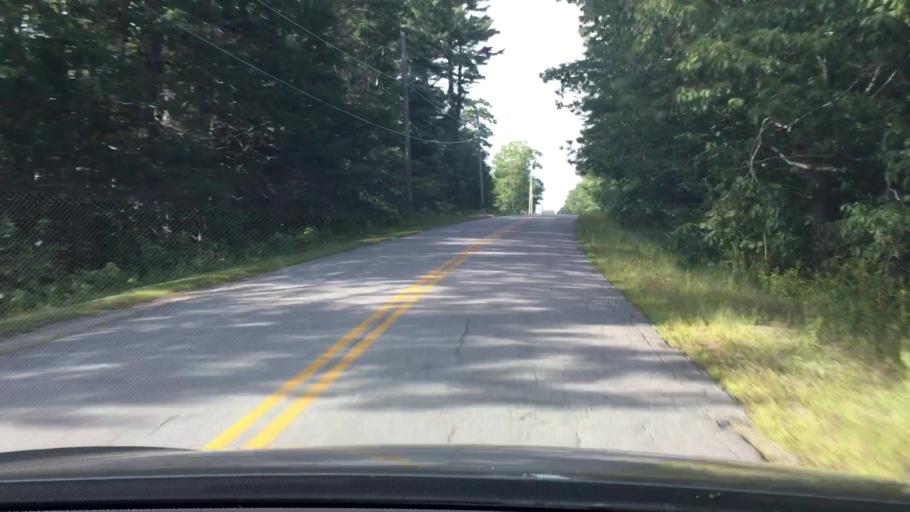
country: US
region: Maine
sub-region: Hancock County
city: Orland
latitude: 44.5237
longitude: -68.7642
